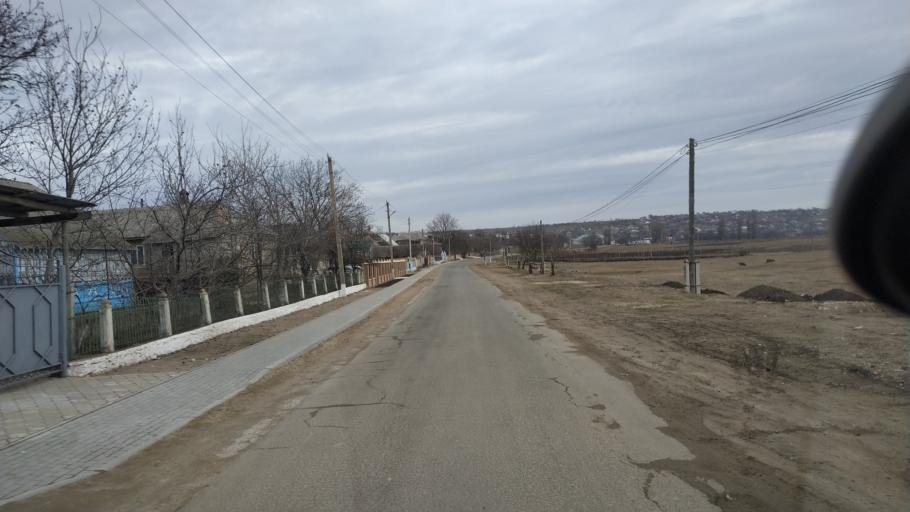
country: MD
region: Telenesti
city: Cocieri
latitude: 47.2645
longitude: 29.0478
